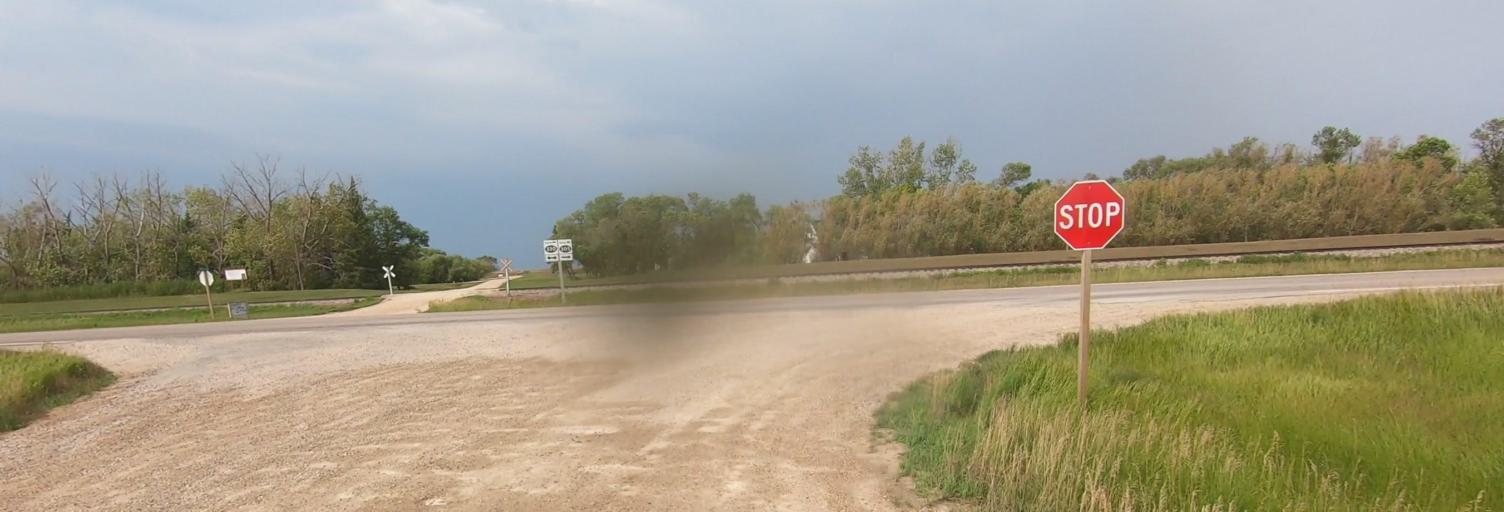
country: CA
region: Manitoba
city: Morris
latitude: 49.5766
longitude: -97.3479
